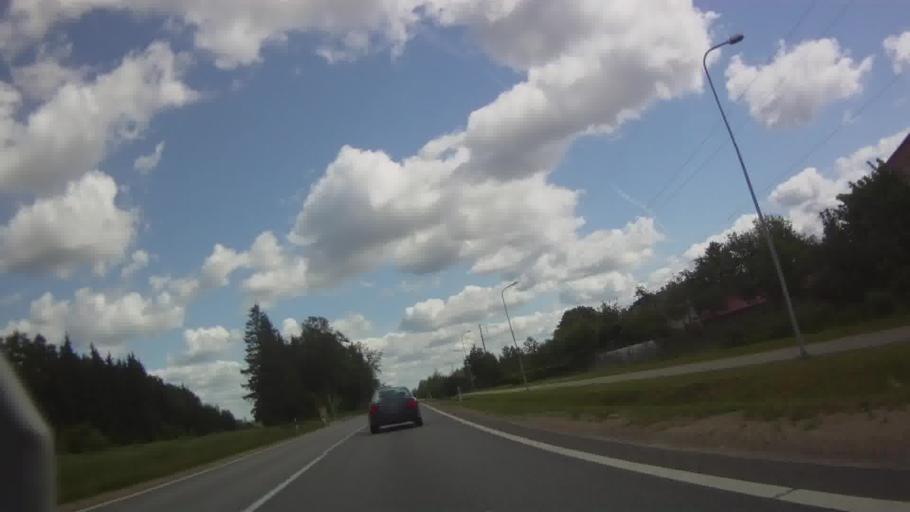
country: LV
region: Jekabpils Rajons
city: Jekabpils
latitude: 56.5242
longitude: 25.9699
